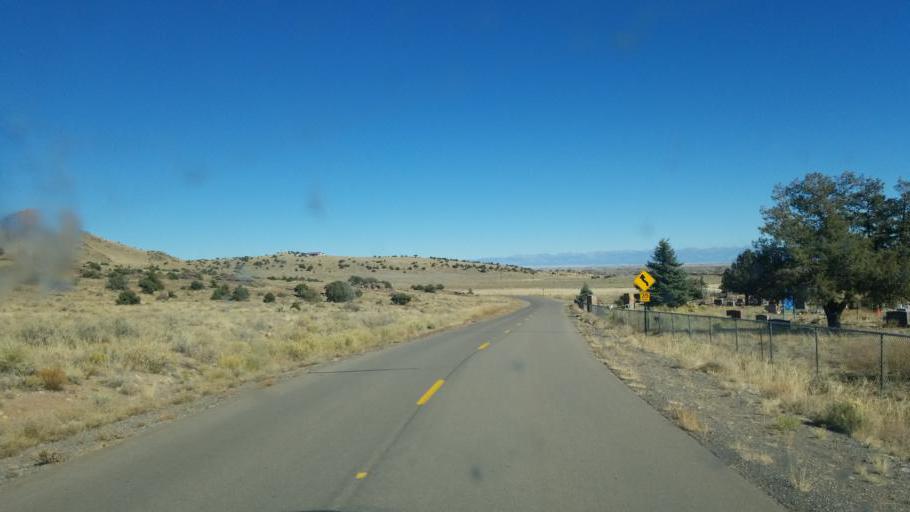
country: US
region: Colorado
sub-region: Rio Grande County
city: Del Norte
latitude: 37.6578
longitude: -106.3613
